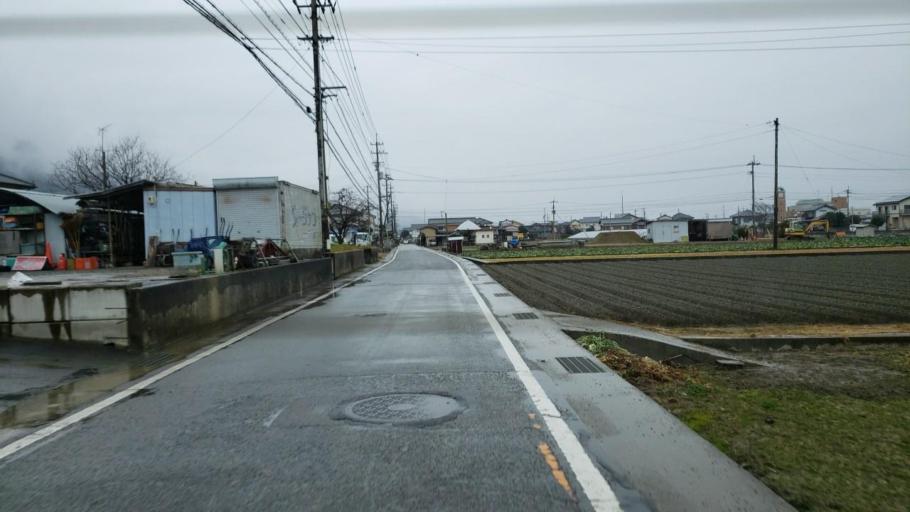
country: JP
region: Tokushima
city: Kamojimacho-jogejima
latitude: 34.0584
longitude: 134.3093
